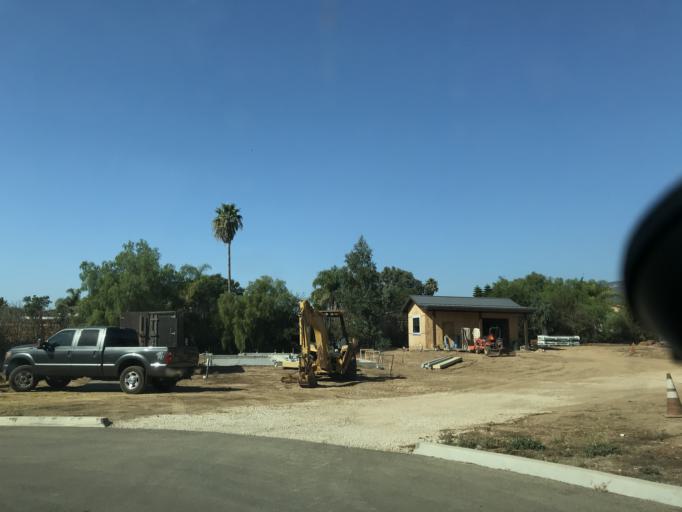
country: US
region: California
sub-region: Santa Barbara County
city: Goleta
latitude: 34.4589
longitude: -119.7874
